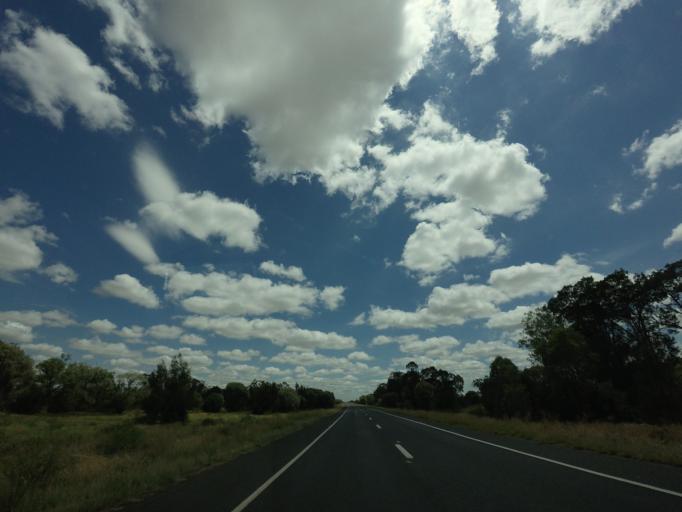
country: AU
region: New South Wales
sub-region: Moree Plains
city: Moree
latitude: -29.1685
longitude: 150.0124
